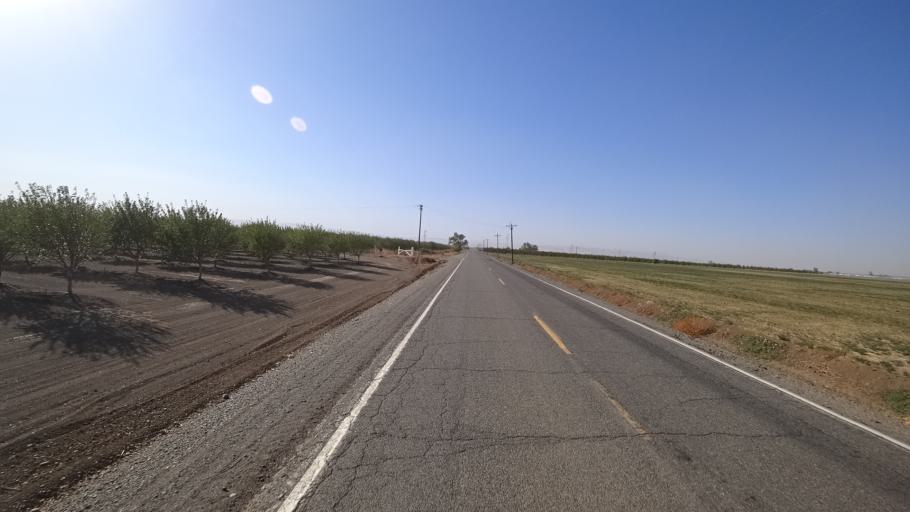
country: US
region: California
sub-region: Yolo County
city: Cottonwood
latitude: 38.7177
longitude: -121.9461
